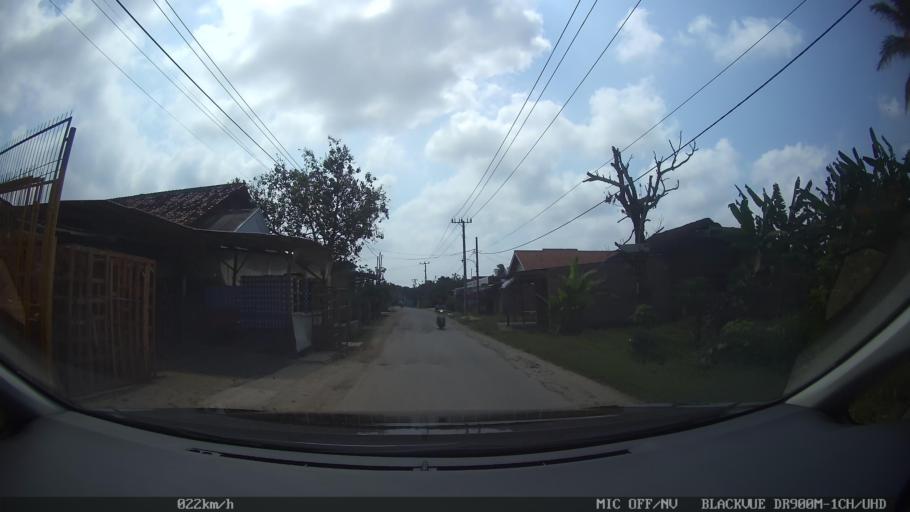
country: ID
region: Lampung
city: Kedaton
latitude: -5.3414
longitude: 105.2834
